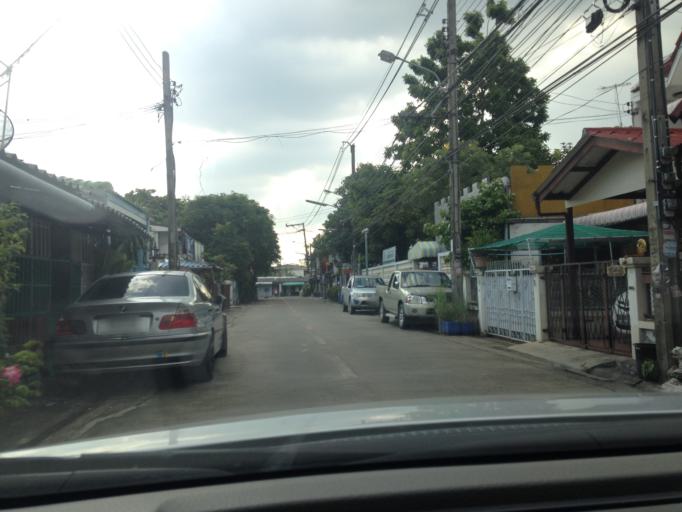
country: TH
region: Bangkok
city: Khan Na Yao
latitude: 13.8427
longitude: 100.6524
